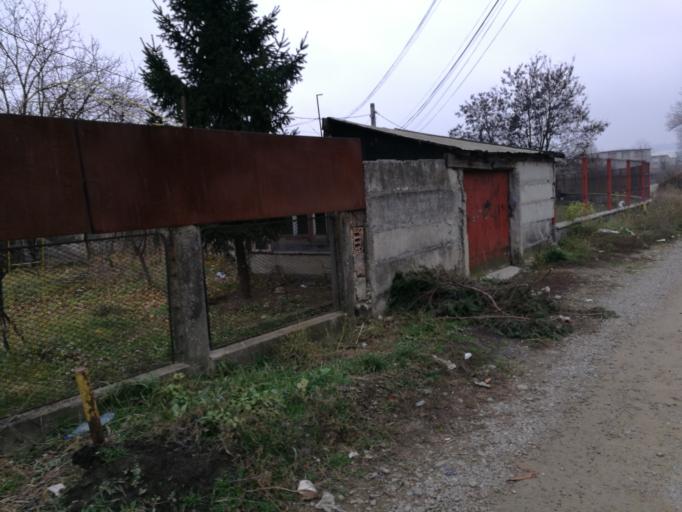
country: RO
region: Suceava
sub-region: Comuna Scheia
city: Scheia
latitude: 47.6739
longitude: 26.2716
